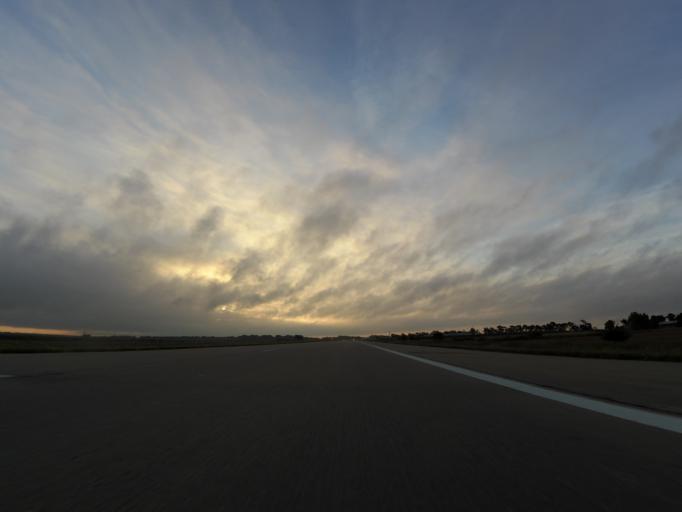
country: US
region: Kansas
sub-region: Reno County
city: Haven
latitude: 37.8796
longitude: -97.7119
